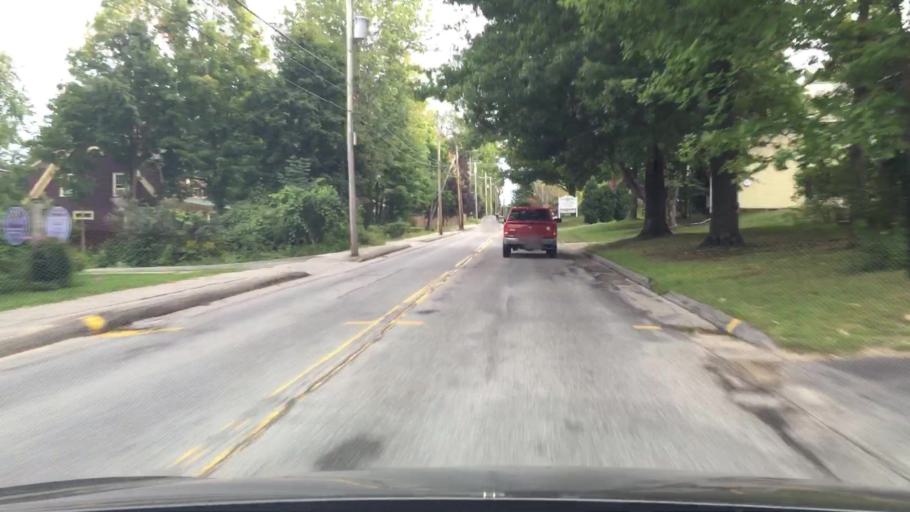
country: US
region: Maine
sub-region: Cumberland County
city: Bridgton
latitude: 44.0524
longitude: -70.7143
